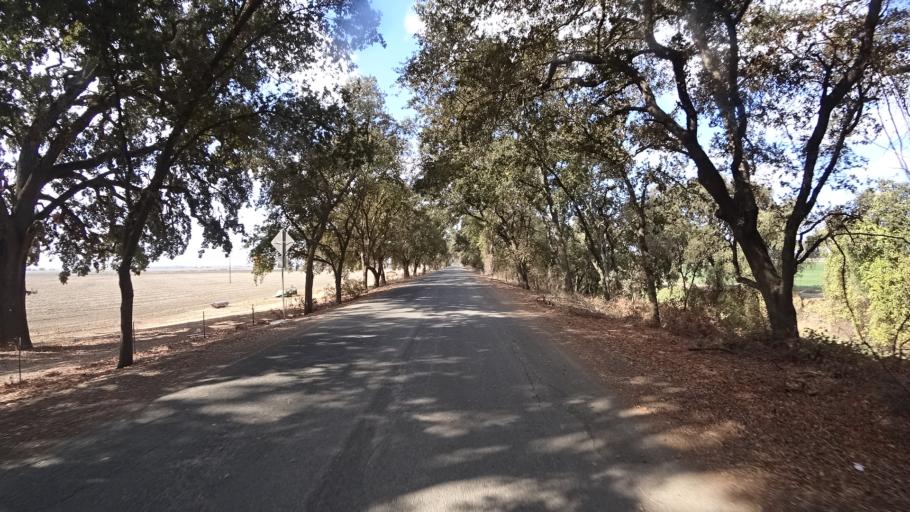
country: US
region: California
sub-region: Yolo County
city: Woodland
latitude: 38.7484
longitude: -121.6794
